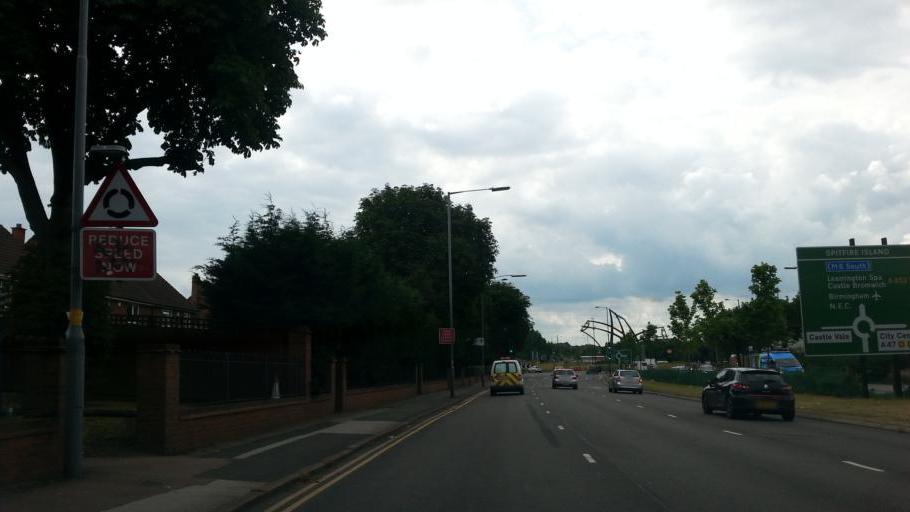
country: GB
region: England
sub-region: City and Borough of Birmingham
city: Sutton Coldfield
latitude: 52.5156
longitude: -1.7985
